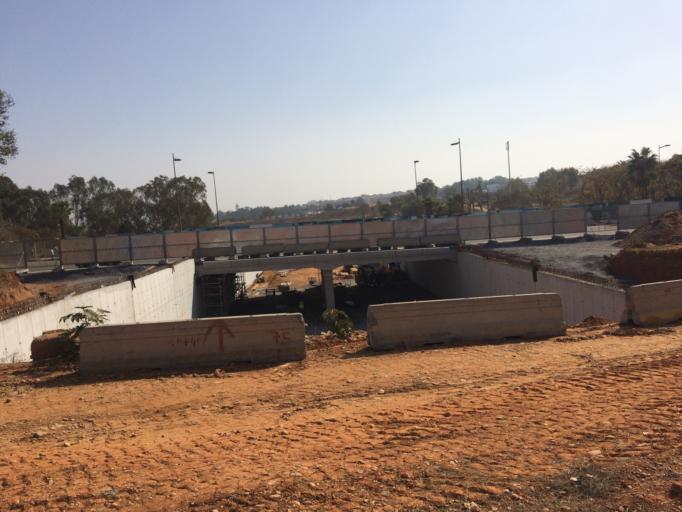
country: MA
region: Rabat-Sale-Zemmour-Zaer
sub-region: Rabat
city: Rabat
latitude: 34.0004
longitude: -6.8282
